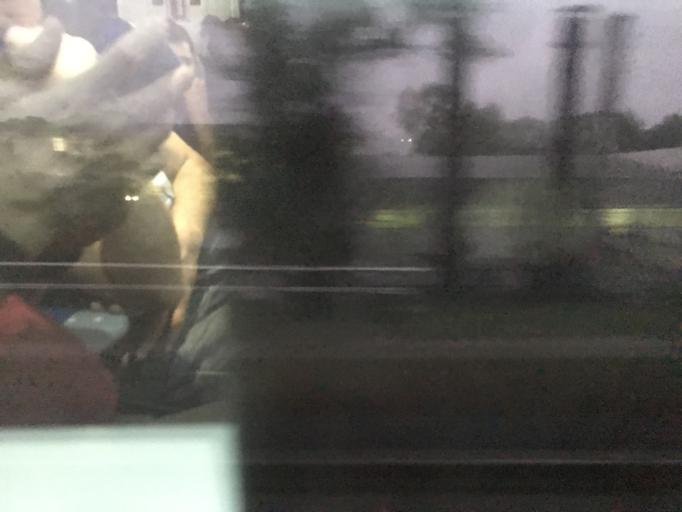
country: TR
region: Kocaeli
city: Derince
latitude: 40.7518
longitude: 29.8212
